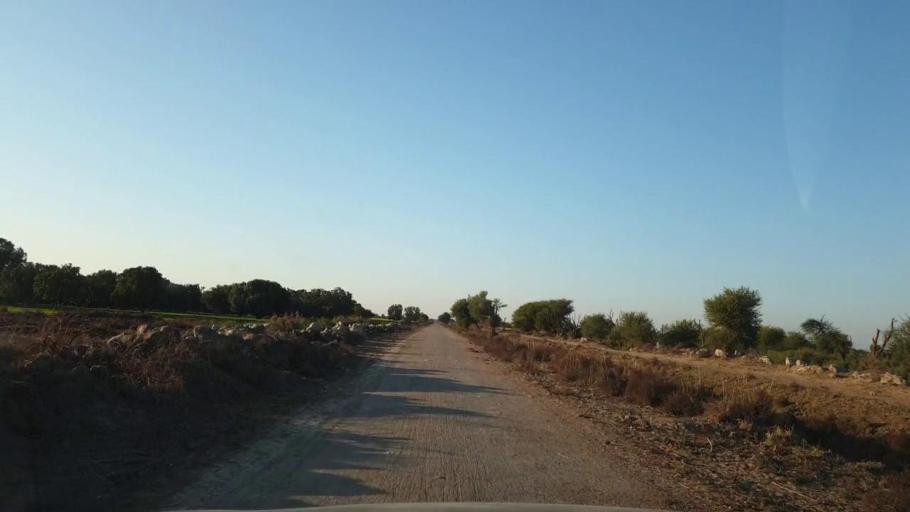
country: PK
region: Sindh
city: Jhol
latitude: 25.8822
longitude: 68.9016
